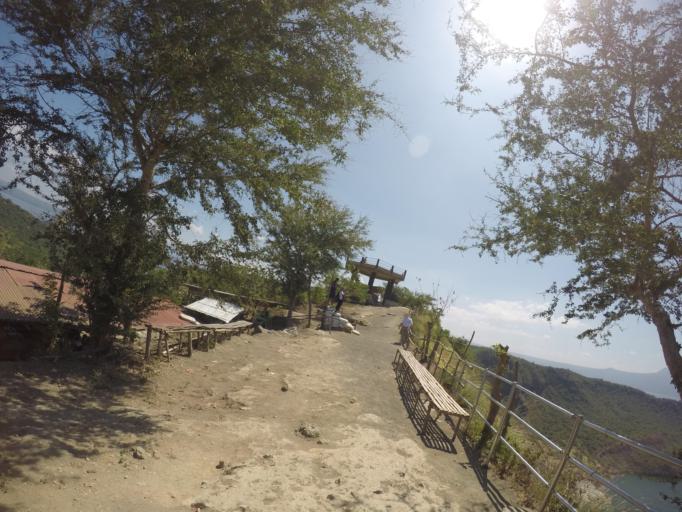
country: PH
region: Calabarzon
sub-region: Province of Batangas
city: Bugaan
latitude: 14.0179
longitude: 120.9993
